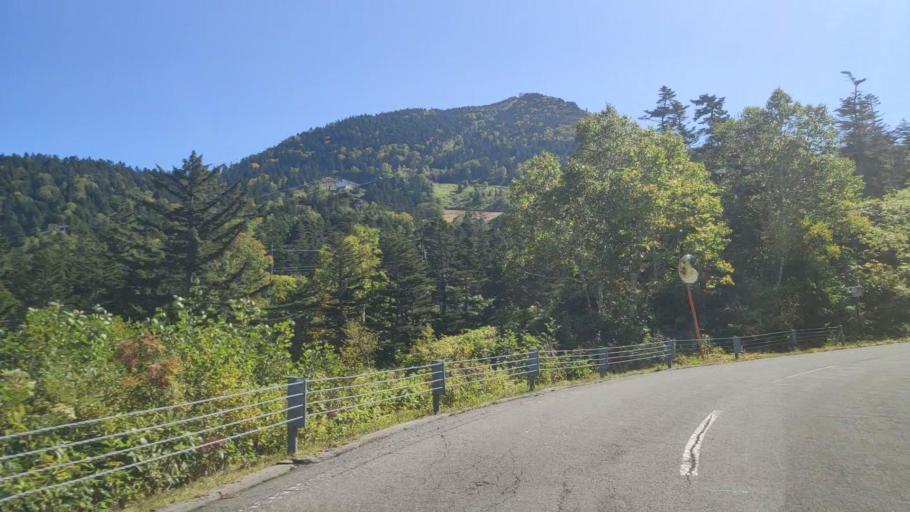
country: JP
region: Nagano
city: Nakano
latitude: 36.6716
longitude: 138.5142
